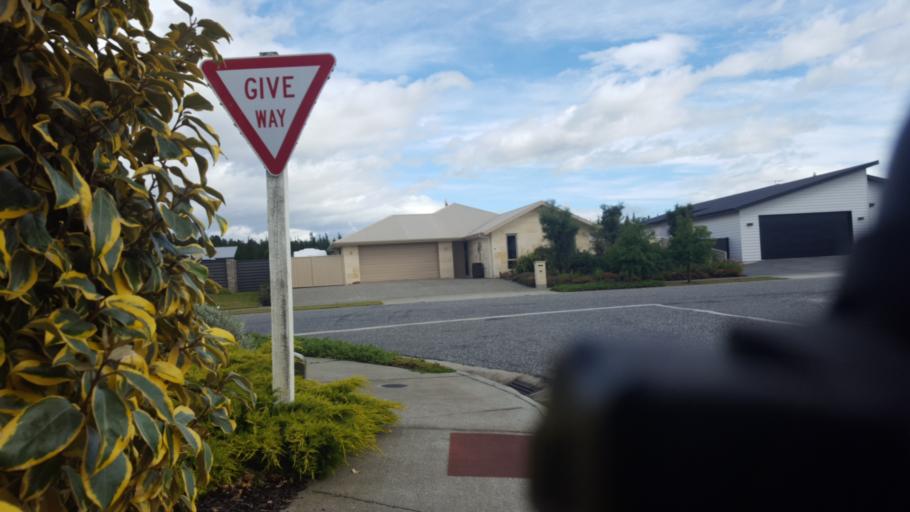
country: NZ
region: Otago
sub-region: Queenstown-Lakes District
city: Wanaka
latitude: -45.2395
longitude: 169.3805
